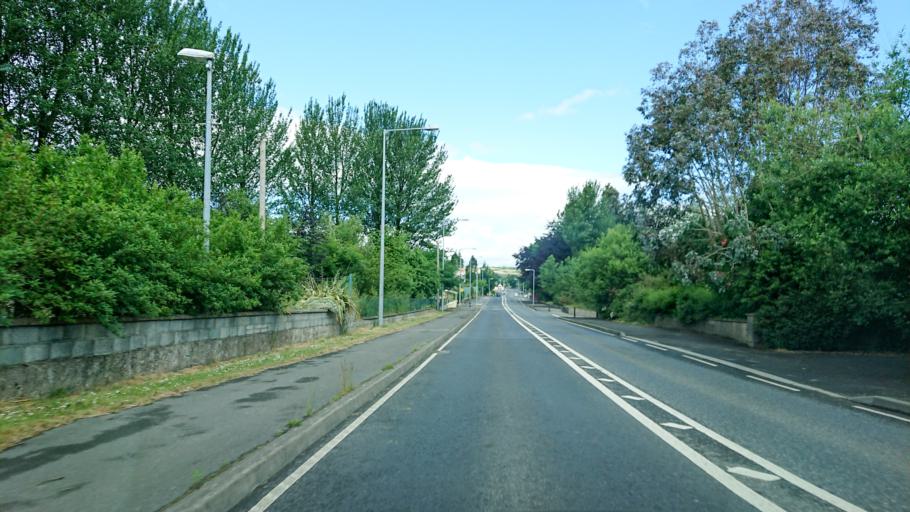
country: IE
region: Leinster
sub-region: Kilkenny
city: Mooncoin
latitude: 52.2311
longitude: -7.2401
